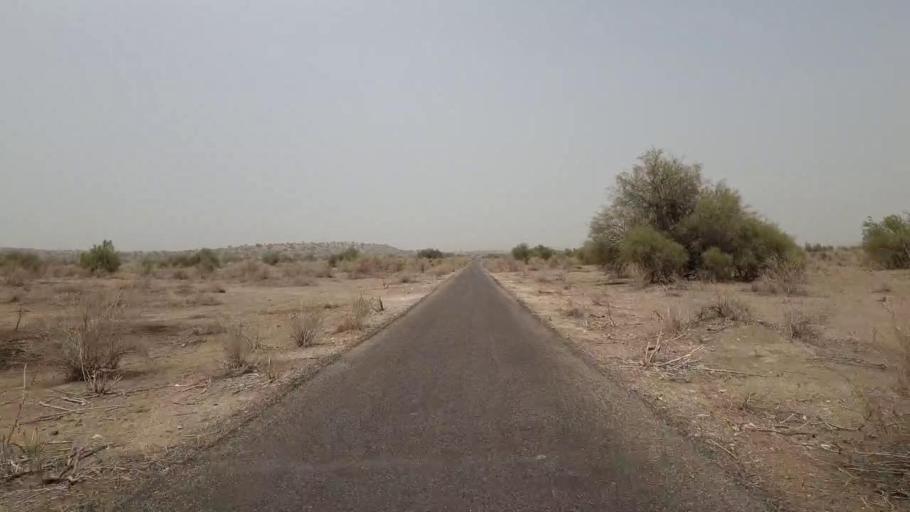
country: PK
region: Sindh
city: Islamkot
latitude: 24.7724
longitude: 70.4899
